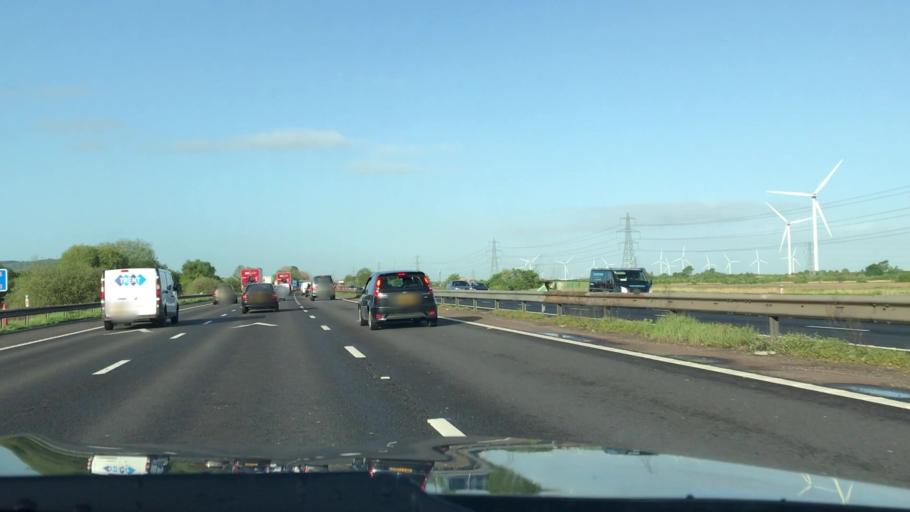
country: GB
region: England
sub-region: Cheshire West and Chester
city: Frodsham
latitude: 53.3004
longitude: -2.7251
